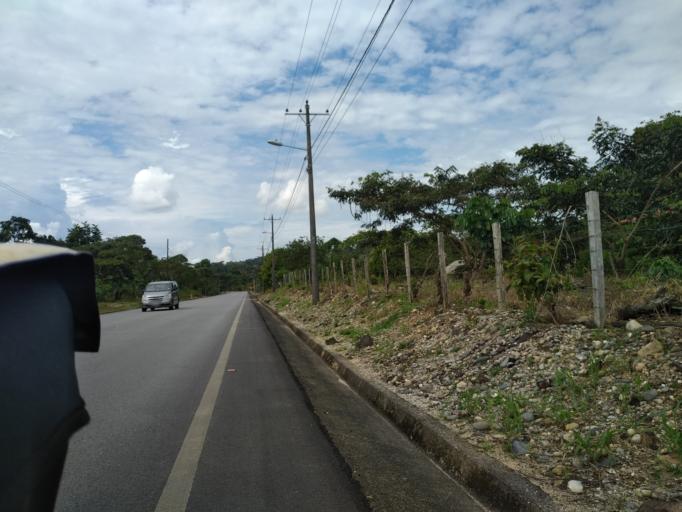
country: EC
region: Napo
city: Tena
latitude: -1.1294
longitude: -77.8247
